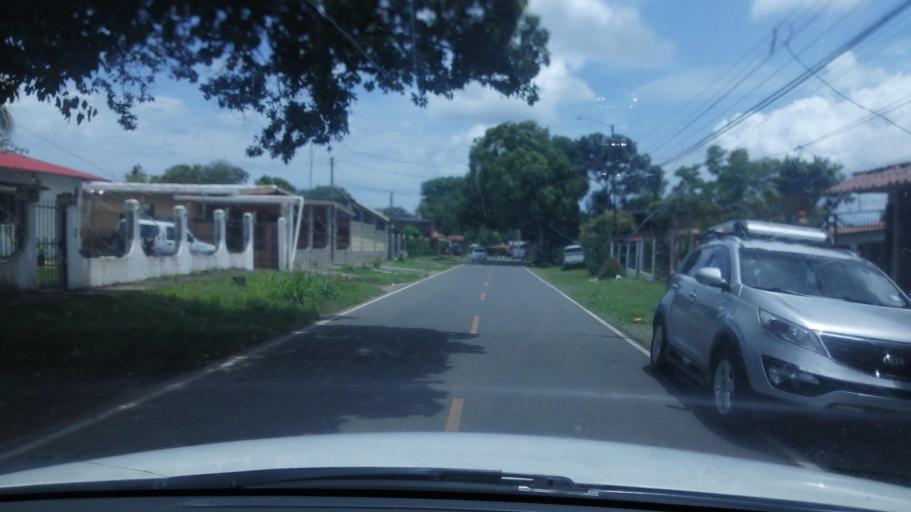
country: PA
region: Chiriqui
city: David
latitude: 8.4204
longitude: -82.4263
